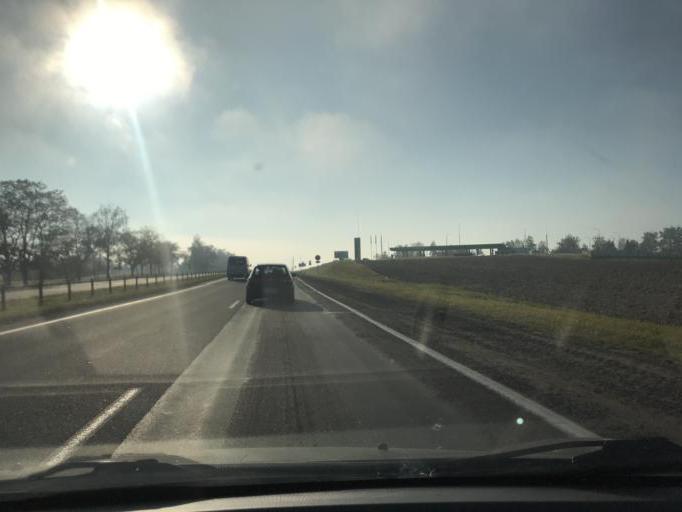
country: BY
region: Minsk
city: Dukora
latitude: 53.7083
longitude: 27.8751
